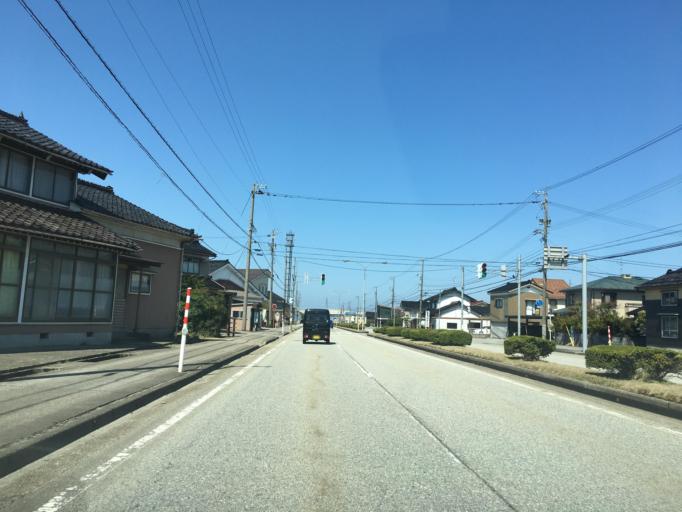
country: JP
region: Toyama
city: Namerikawa
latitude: 36.7505
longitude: 137.3695
